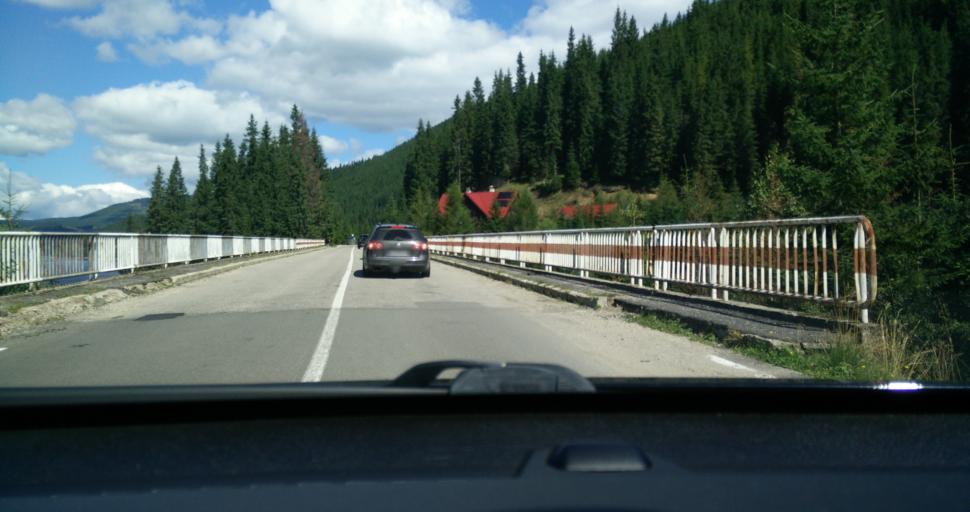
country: RO
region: Alba
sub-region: Comuna Sugag
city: Sugag
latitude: 45.5399
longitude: 23.6388
